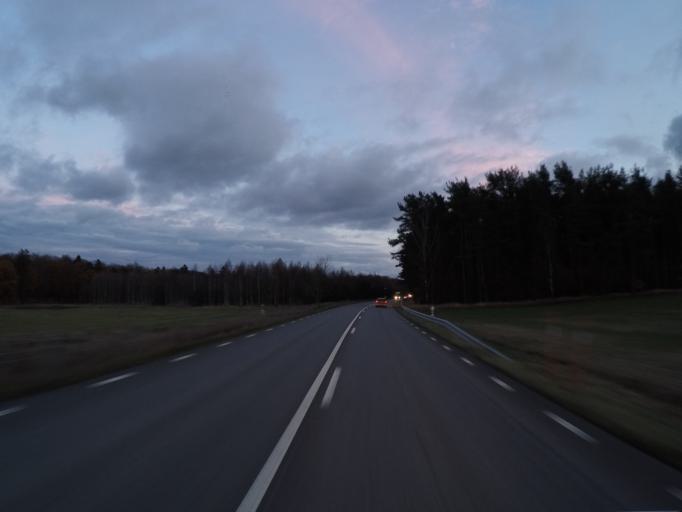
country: SE
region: Skane
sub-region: Kristianstads Kommun
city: Degeberga
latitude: 55.8176
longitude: 14.1281
